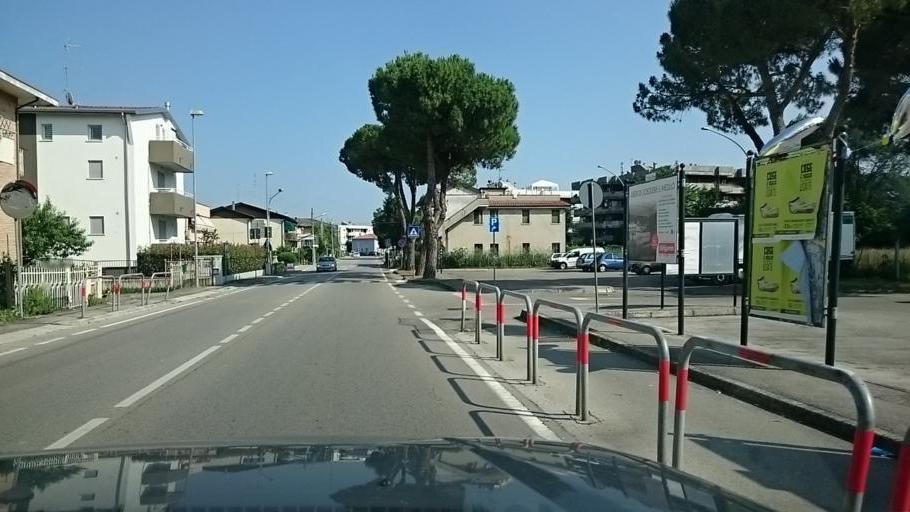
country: IT
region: Veneto
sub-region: Provincia di Padova
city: Vigodarzere
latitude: 45.4515
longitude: 11.8922
